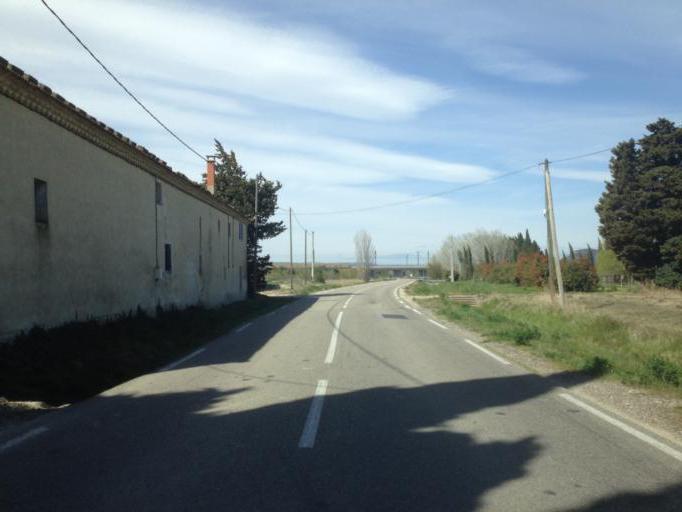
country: FR
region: Provence-Alpes-Cote d'Azur
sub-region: Departement du Vaucluse
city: Caderousse
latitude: 44.1386
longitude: 4.7677
